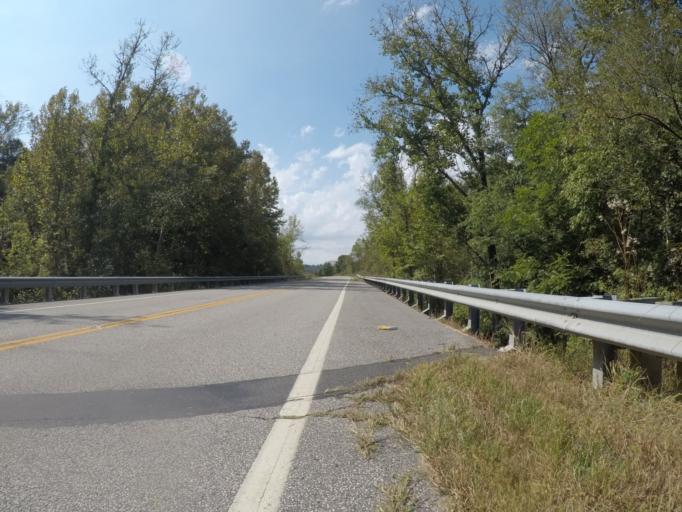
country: US
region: West Virginia
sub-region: Cabell County
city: Lesage
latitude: 38.5152
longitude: -82.3908
